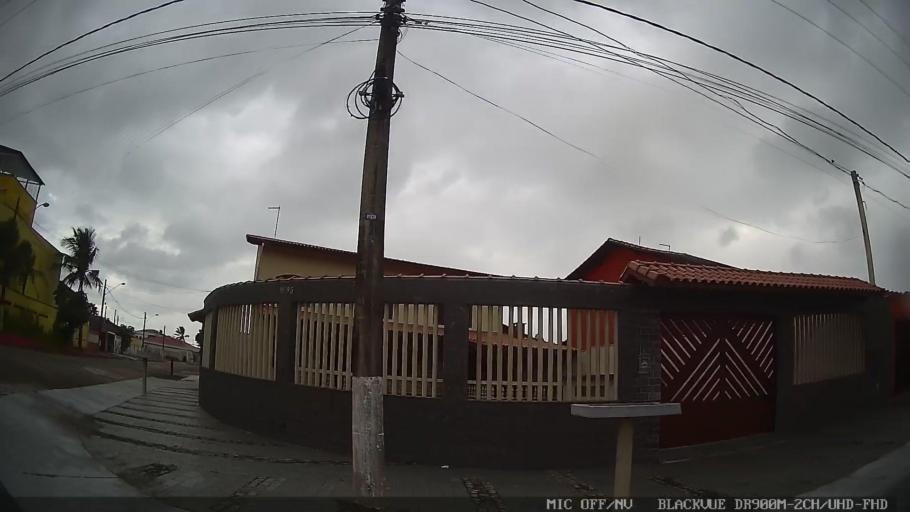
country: BR
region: Sao Paulo
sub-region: Itanhaem
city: Itanhaem
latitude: -24.1392
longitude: -46.7065
